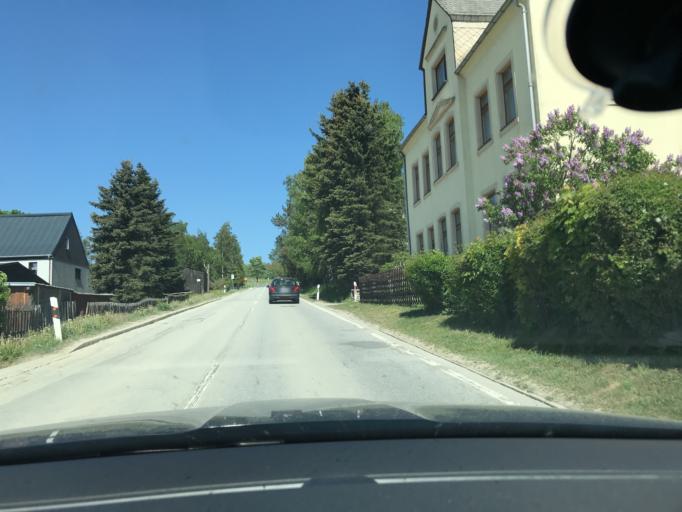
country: CZ
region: Ustecky
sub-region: Okres Chomutov
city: Kovarska
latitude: 50.4462
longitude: 13.0138
